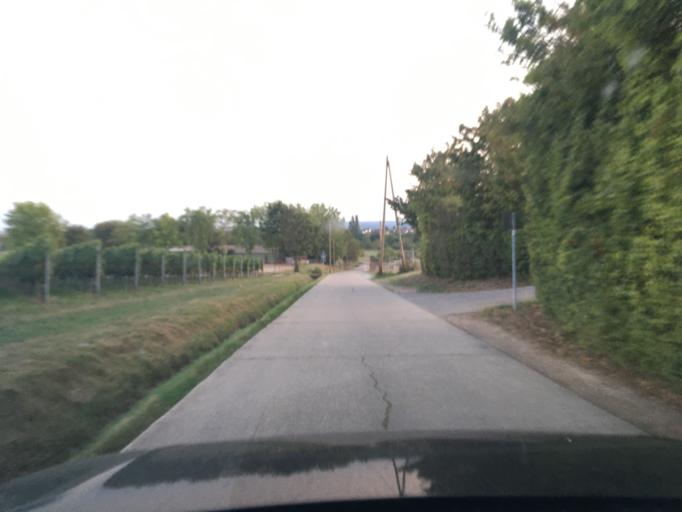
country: DE
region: Baden-Wuerttemberg
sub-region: Regierungsbezirk Stuttgart
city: Brackenheim
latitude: 49.0961
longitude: 9.0797
